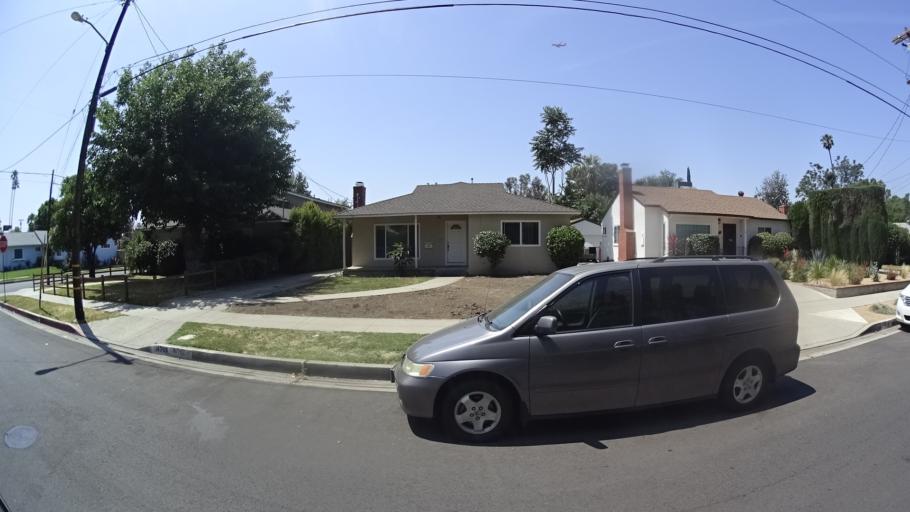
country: US
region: California
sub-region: Los Angeles County
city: Van Nuys
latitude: 34.2066
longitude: -118.4534
